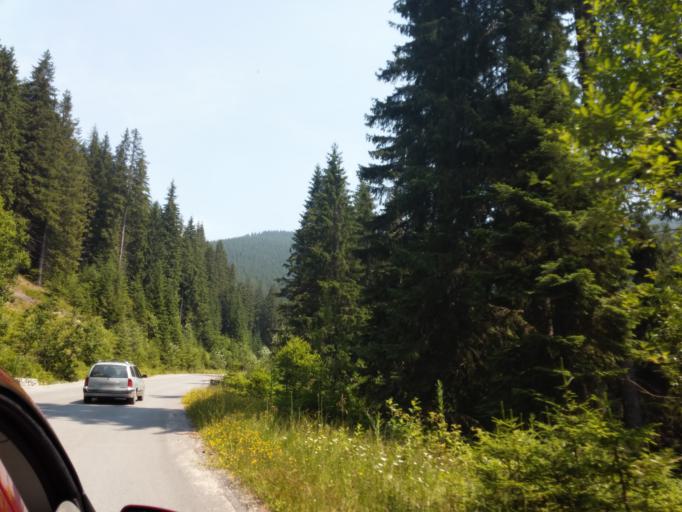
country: RO
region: Valcea
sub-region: Comuna Voineasa
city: Voineasa
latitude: 45.4247
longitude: 23.7759
